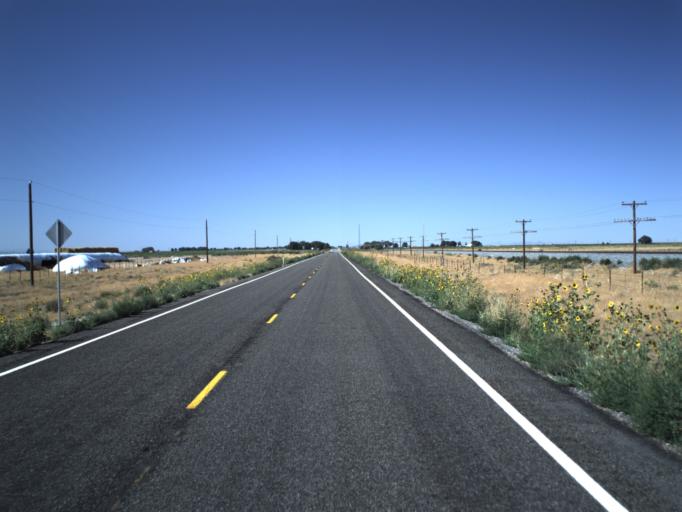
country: US
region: Utah
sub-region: Millard County
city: Delta
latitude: 39.5580
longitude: -112.3517
